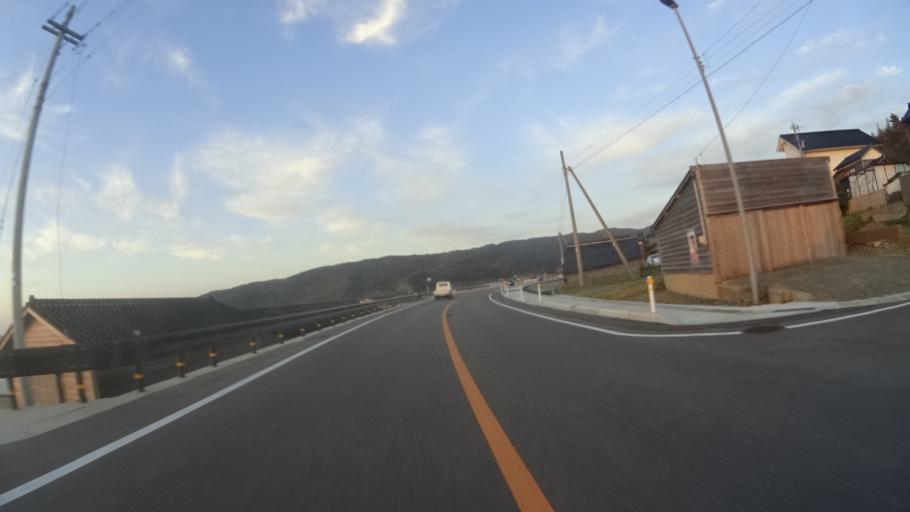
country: JP
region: Ishikawa
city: Nanao
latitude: 37.2815
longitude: 136.7336
